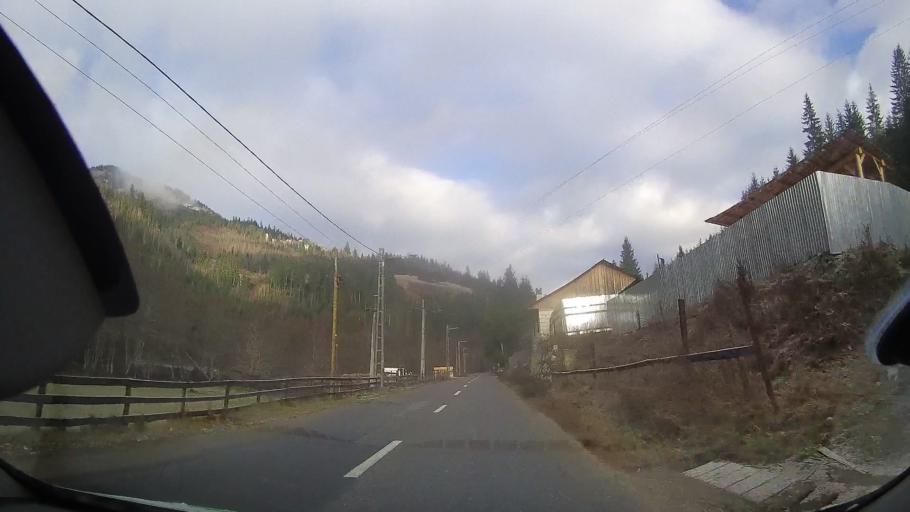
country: RO
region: Alba
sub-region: Comuna Albac
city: Albac
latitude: 46.4643
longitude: 22.9687
